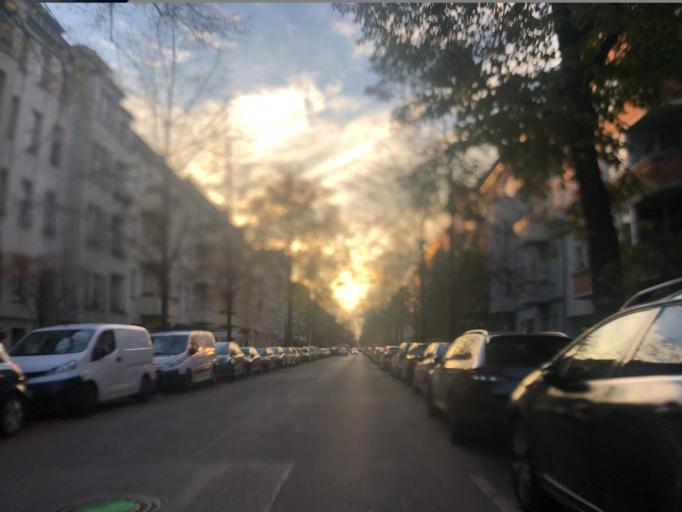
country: DE
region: Berlin
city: Weissensee
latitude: 52.5504
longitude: 13.4656
